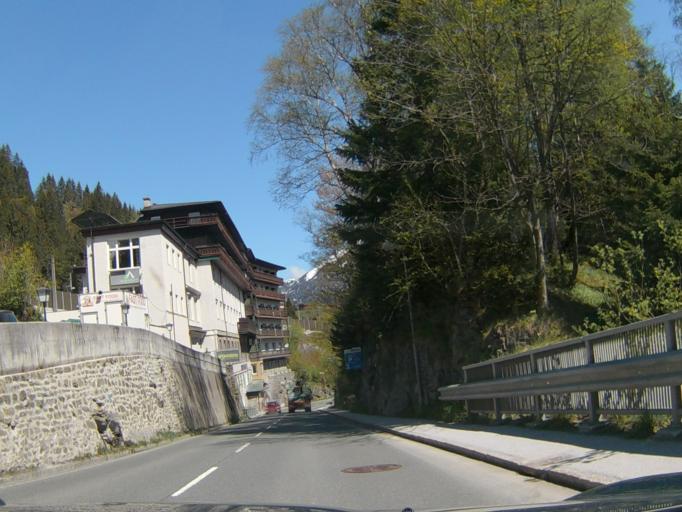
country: AT
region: Salzburg
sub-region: Politischer Bezirk Sankt Johann im Pongau
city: Bad Gastein
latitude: 47.1137
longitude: 13.1322
